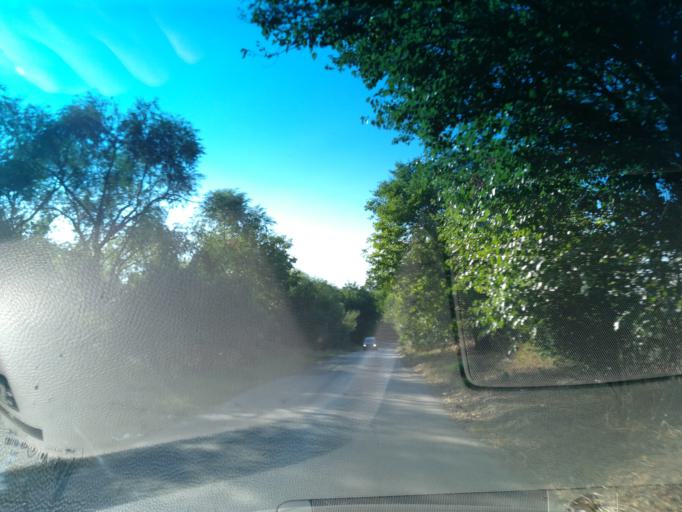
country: BG
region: Stara Zagora
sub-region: Obshtina Chirpan
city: Chirpan
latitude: 42.0566
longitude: 25.2686
